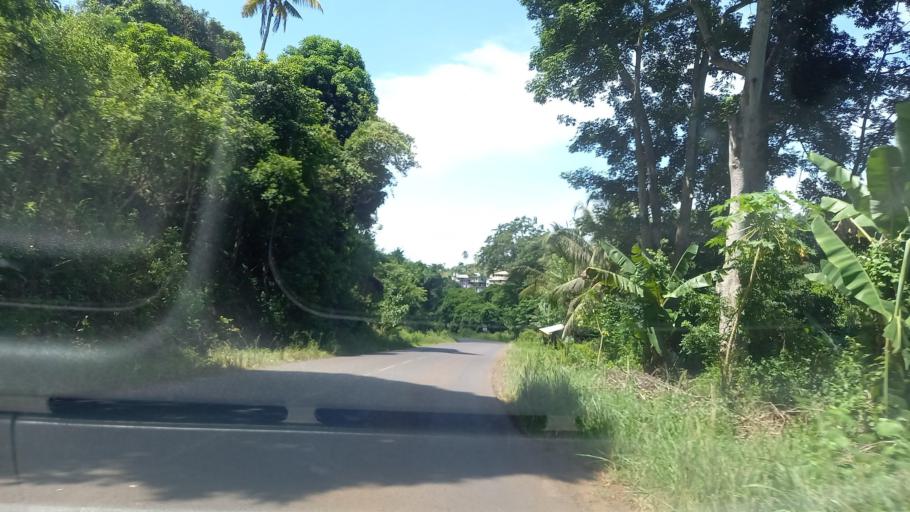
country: YT
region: M'Tsangamouji
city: M'Tsangamouji
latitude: -12.7547
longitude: 45.0903
